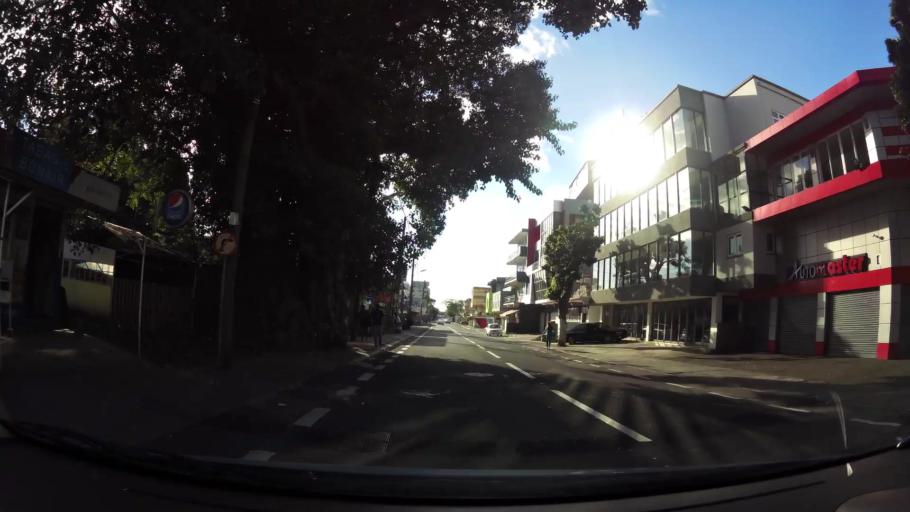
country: MU
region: Plaines Wilhems
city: Ebene
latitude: -20.2535
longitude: 57.4857
